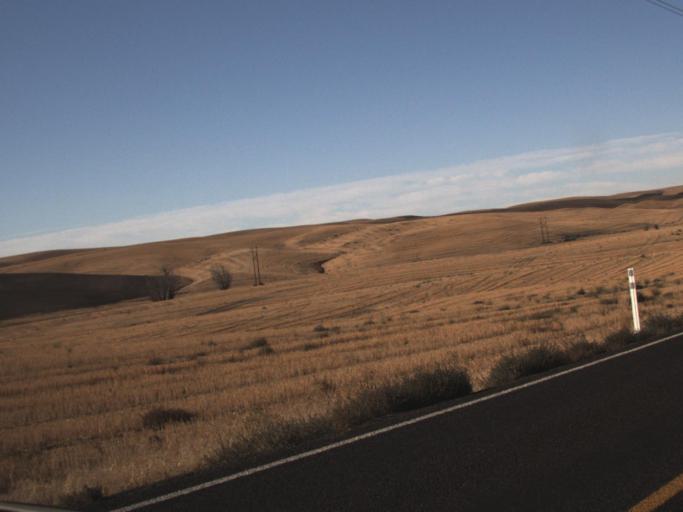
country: US
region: Washington
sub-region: Walla Walla County
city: Walla Walla
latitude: 46.1574
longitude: -118.3792
